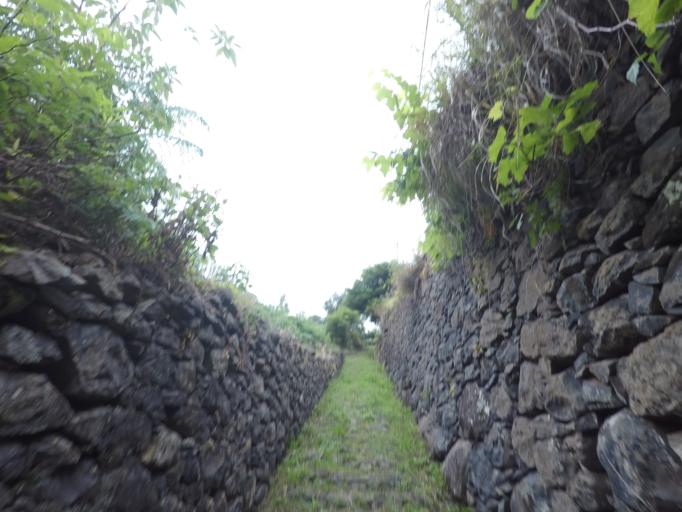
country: PT
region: Madeira
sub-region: Santana
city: Santana
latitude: 32.7644
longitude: -16.8308
